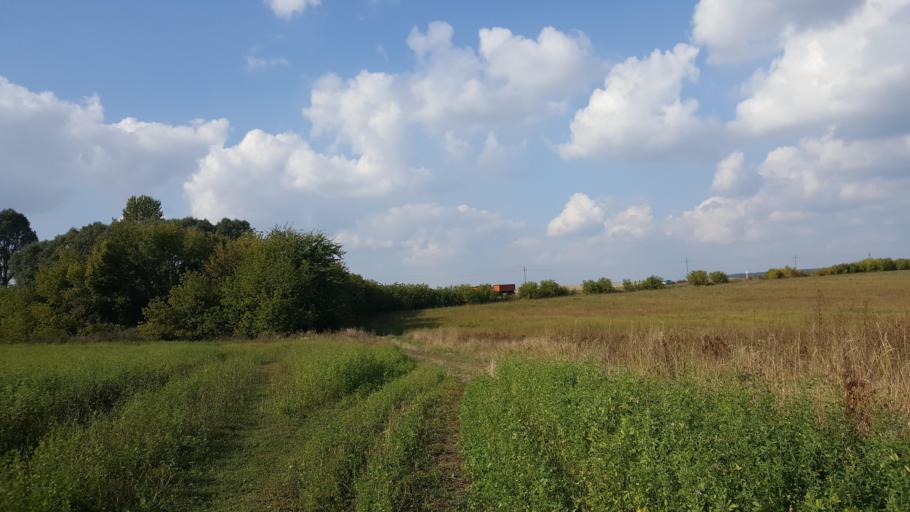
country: BY
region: Brest
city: Kamyanyets
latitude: 52.4224
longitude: 23.8125
